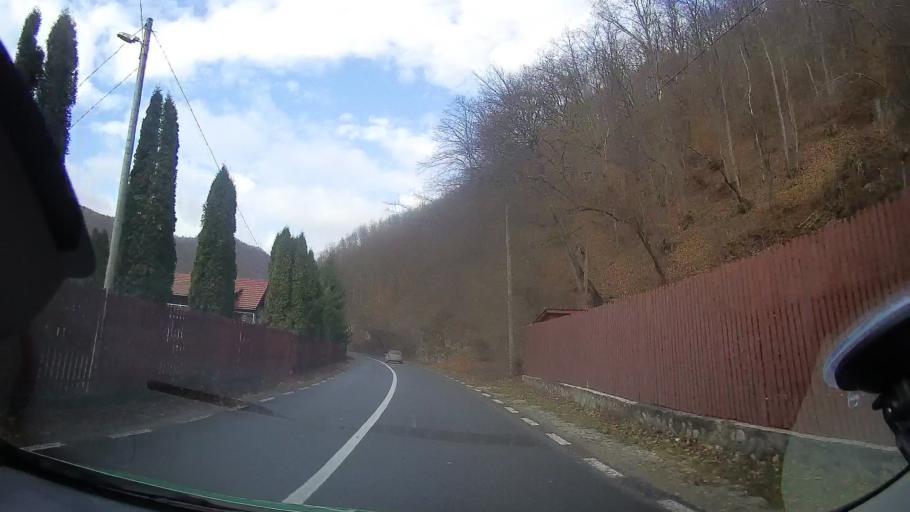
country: RO
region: Cluj
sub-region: Comuna Valea Ierii
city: Valea Ierii
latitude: 46.6135
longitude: 23.4056
